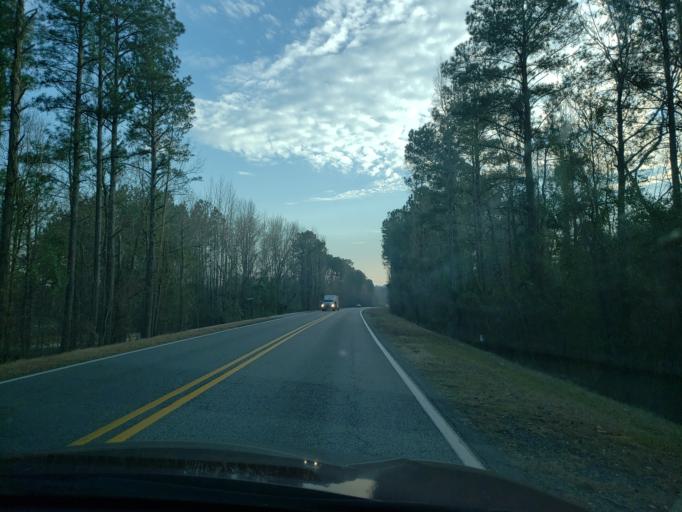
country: US
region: Alabama
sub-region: Hale County
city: Greensboro
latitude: 32.7311
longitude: -87.5873
